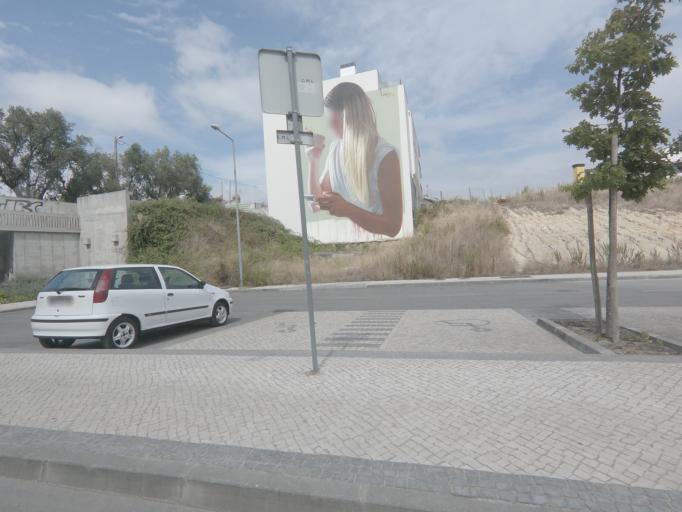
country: PT
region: Leiria
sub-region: Leiria
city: Leiria
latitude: 39.7440
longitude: -8.8129
